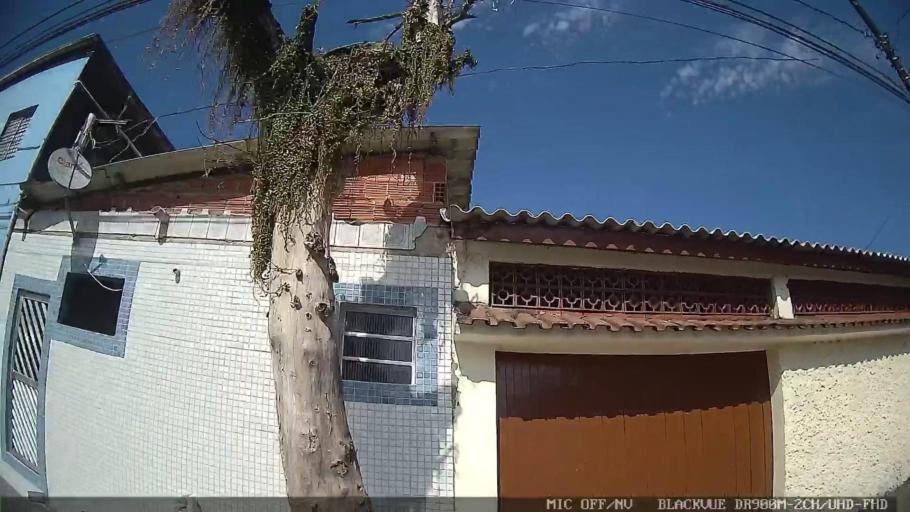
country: BR
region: Sao Paulo
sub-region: Santos
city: Santos
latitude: -23.9464
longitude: -46.2961
